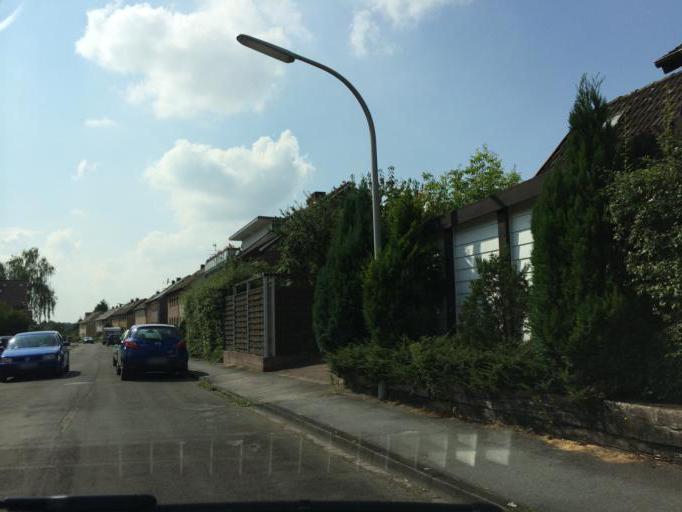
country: DE
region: North Rhine-Westphalia
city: Dorsten
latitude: 51.6673
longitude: 6.9807
